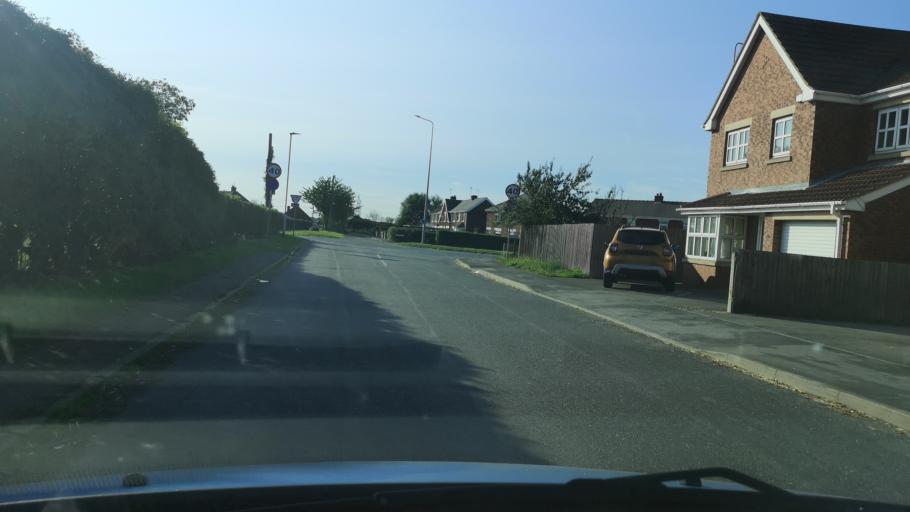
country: GB
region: England
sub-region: North Lincolnshire
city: Gunness
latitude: 53.5780
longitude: -0.7433
